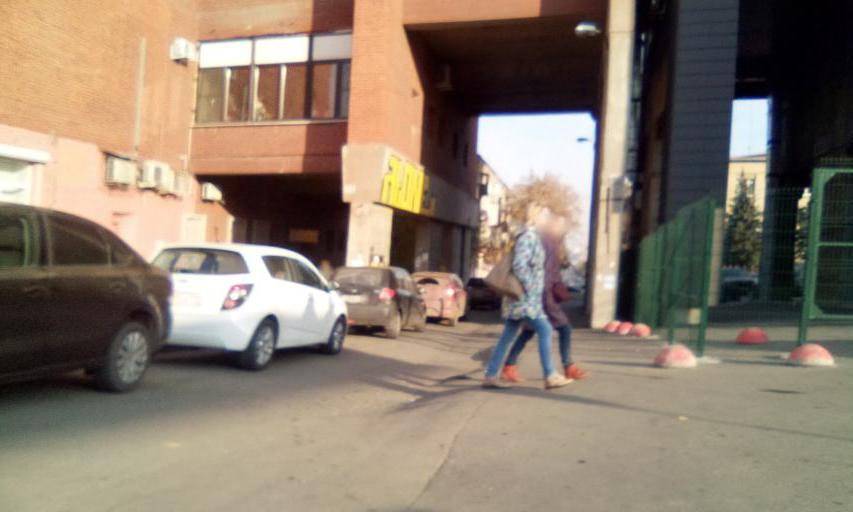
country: RU
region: Chelyabinsk
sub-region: Gorod Chelyabinsk
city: Chelyabinsk
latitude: 55.1582
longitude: 61.3963
